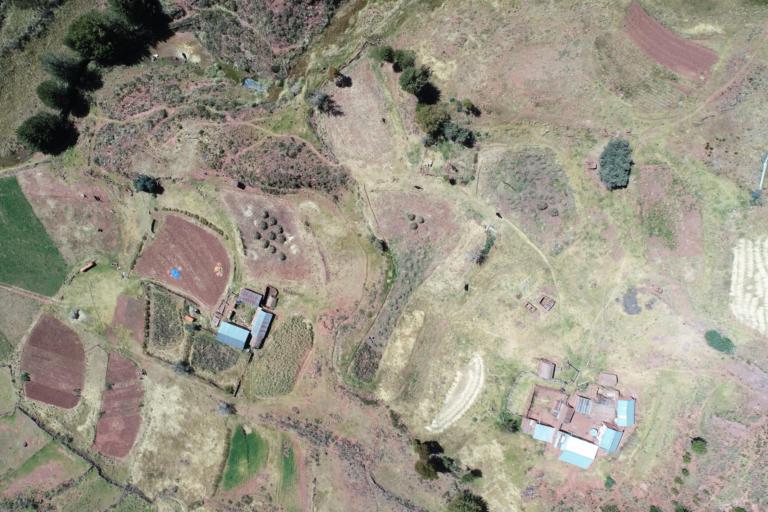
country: BO
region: La Paz
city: Tiahuanaco
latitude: -16.6064
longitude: -68.7638
